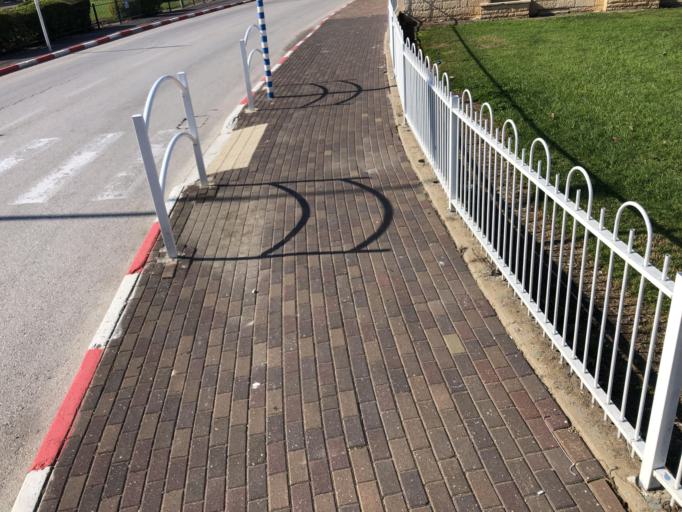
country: IL
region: Northern District
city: `Akko
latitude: 32.9217
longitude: 35.0938
